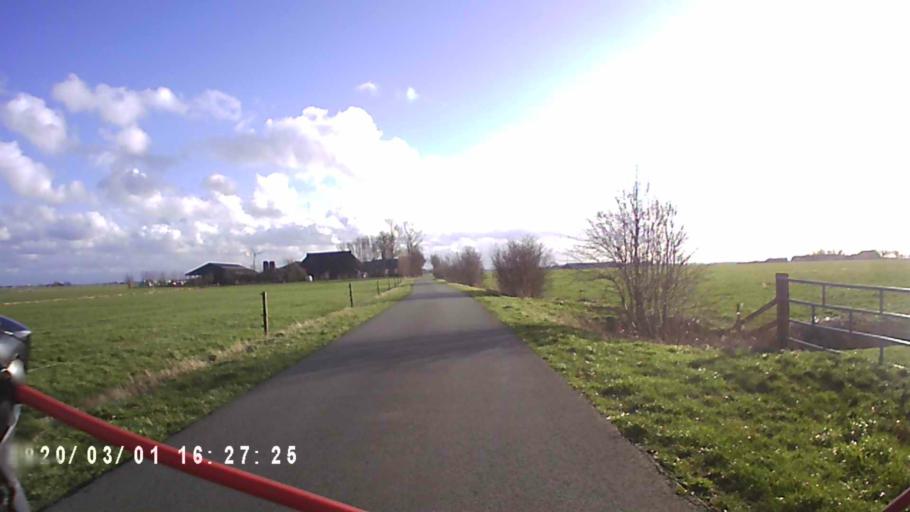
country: NL
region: Groningen
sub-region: Gemeente Zuidhorn
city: Oldehove
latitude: 53.3065
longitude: 6.4290
